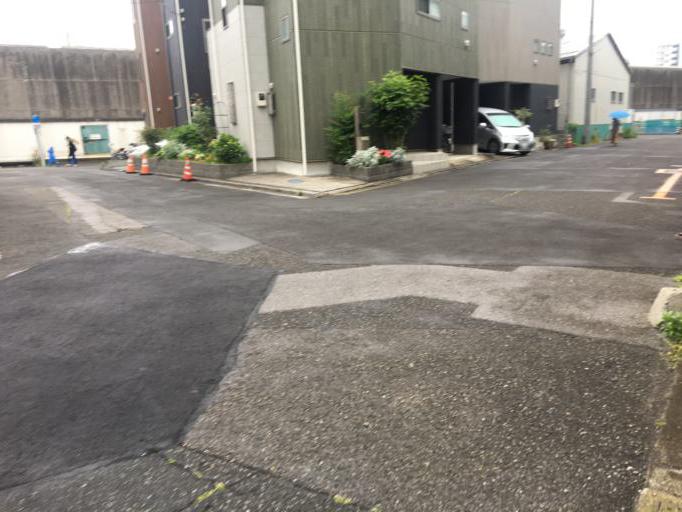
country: JP
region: Saitama
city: Shimotoda
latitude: 35.8459
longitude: 139.6605
